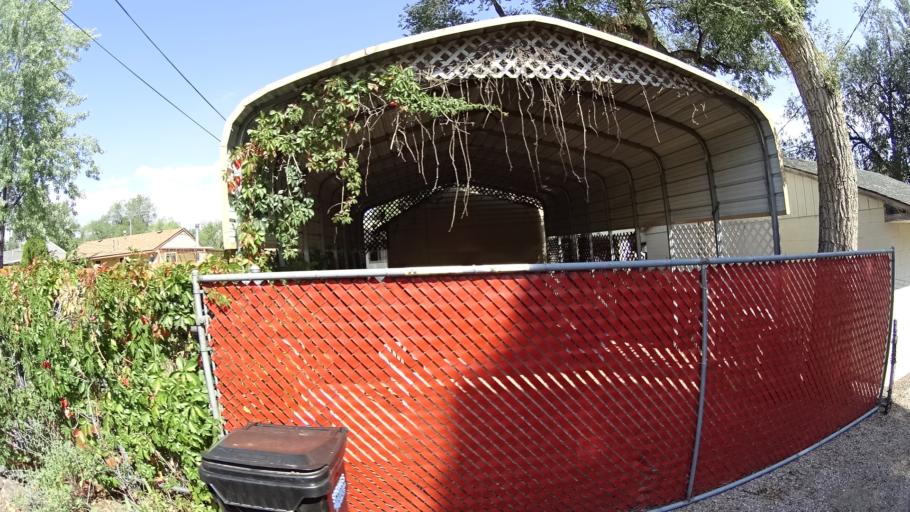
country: US
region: Colorado
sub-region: El Paso County
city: Colorado Springs
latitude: 38.8248
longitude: -104.7900
